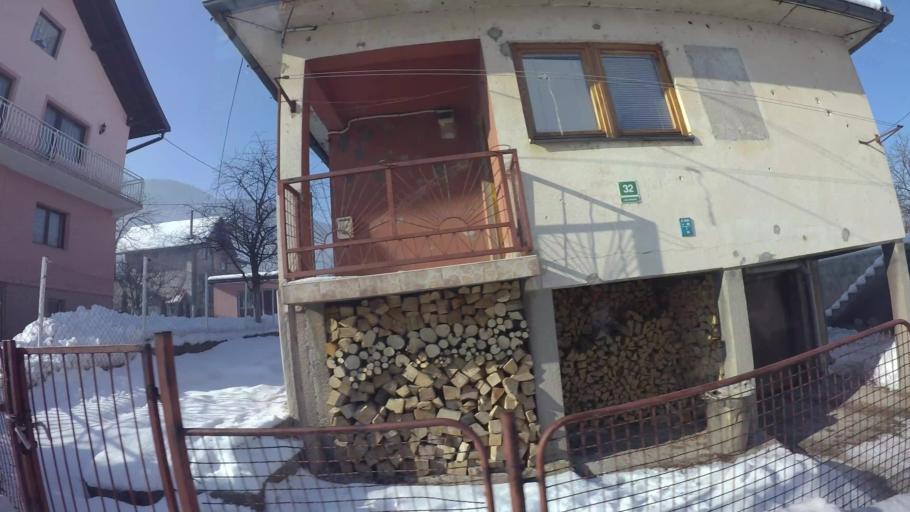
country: BA
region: Federation of Bosnia and Herzegovina
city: Gracanica
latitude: 43.7930
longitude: 18.3165
